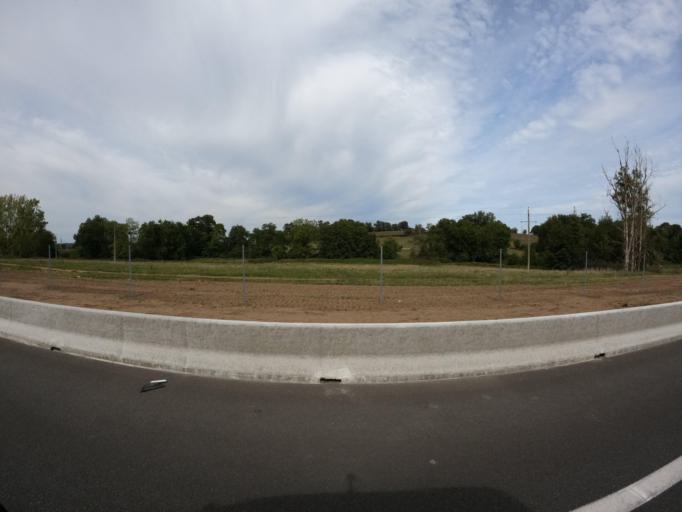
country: FR
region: Auvergne
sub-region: Departement de l'Allier
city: Toulon-sur-Allier
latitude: 46.4977
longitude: 3.3703
